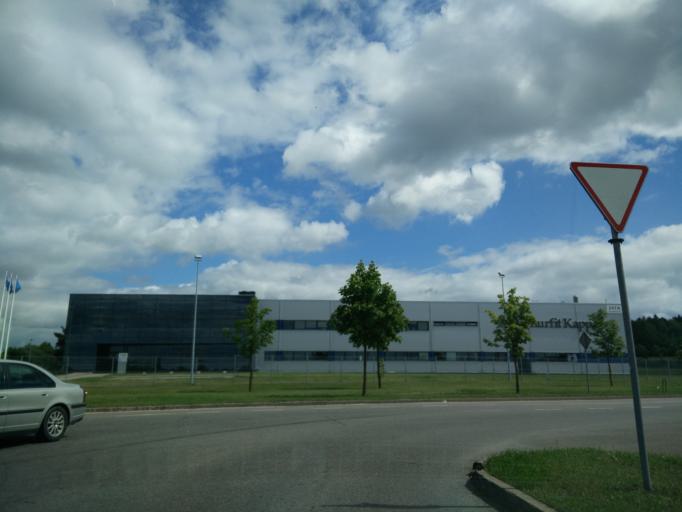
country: LT
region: Vilnius County
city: Pilaite
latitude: 54.6568
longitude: 25.1416
